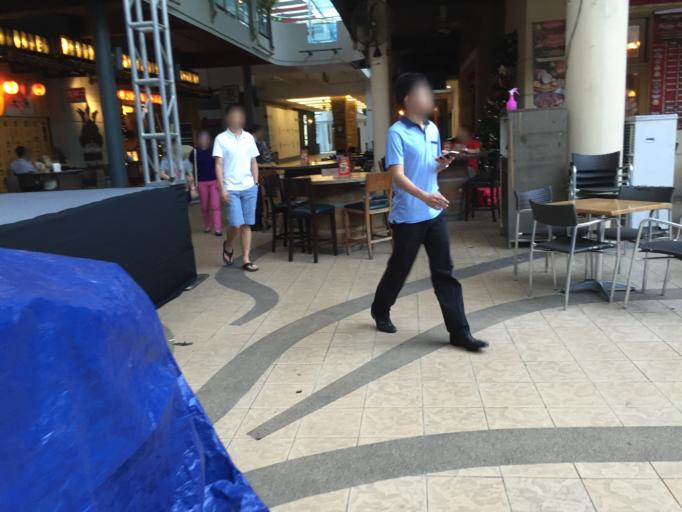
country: MY
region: Selangor
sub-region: Petaling
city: Petaling Jaya
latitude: 3.1178
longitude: 101.6356
